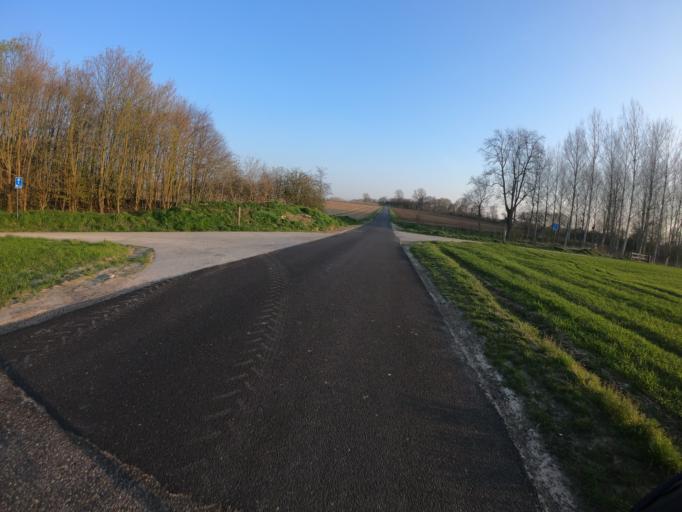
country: BE
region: Flanders
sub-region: Provincie Limburg
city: Kortessem
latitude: 50.8134
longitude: 5.3918
